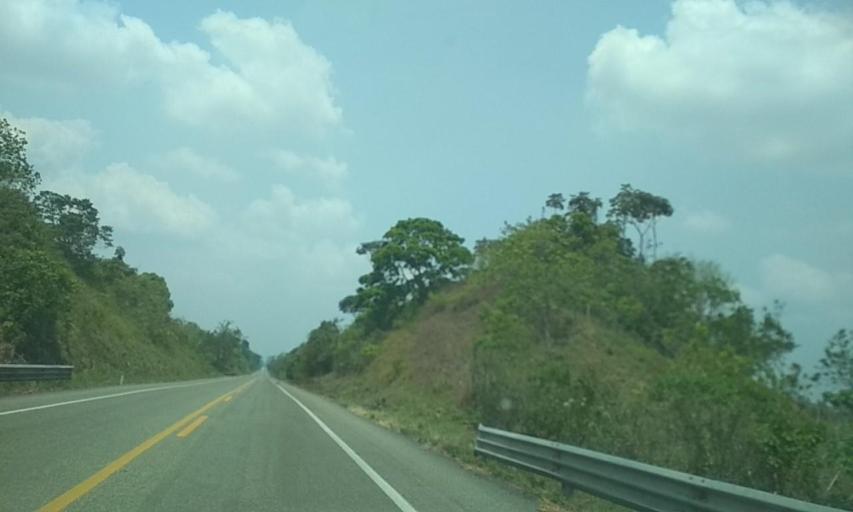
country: MX
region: Tabasco
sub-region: Huimanguillo
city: Francisco Rueda
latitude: 17.6591
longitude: -93.8511
